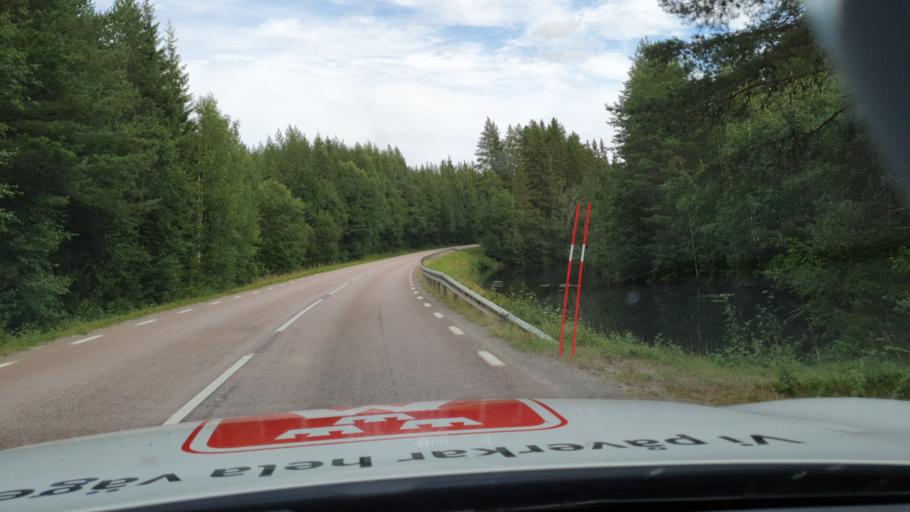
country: SE
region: Vaesternorrland
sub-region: Solleftea Kommun
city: As
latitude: 63.5976
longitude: 16.2615
